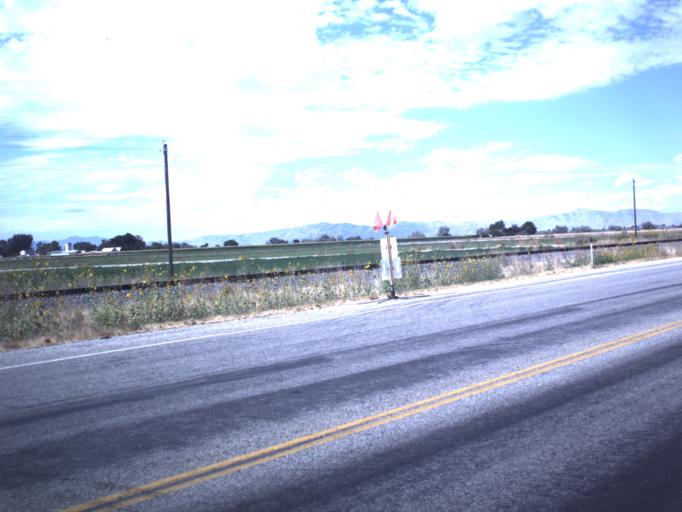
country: US
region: Utah
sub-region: Box Elder County
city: Brigham City
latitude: 41.5364
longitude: -112.0700
